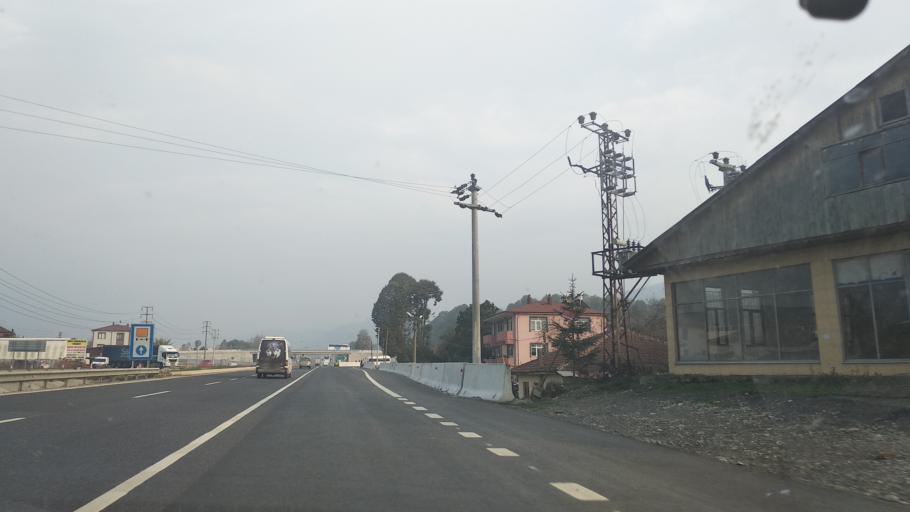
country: TR
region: Duzce
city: Kaynasli
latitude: 40.7833
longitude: 31.2731
